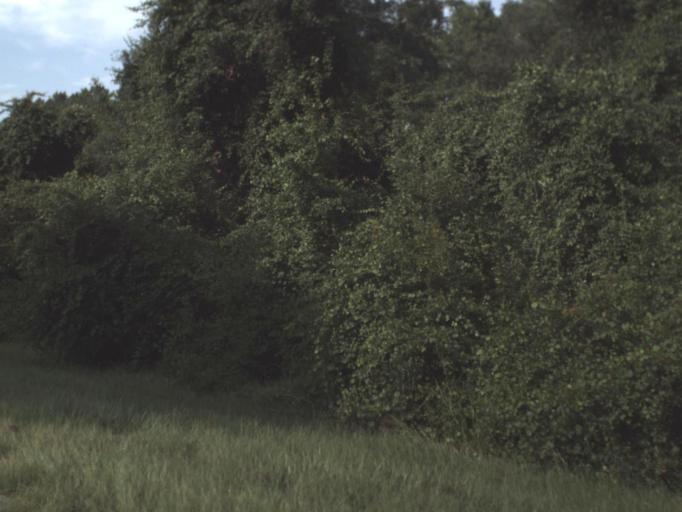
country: US
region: Florida
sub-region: Taylor County
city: Perry
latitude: 30.3293
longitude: -83.6435
